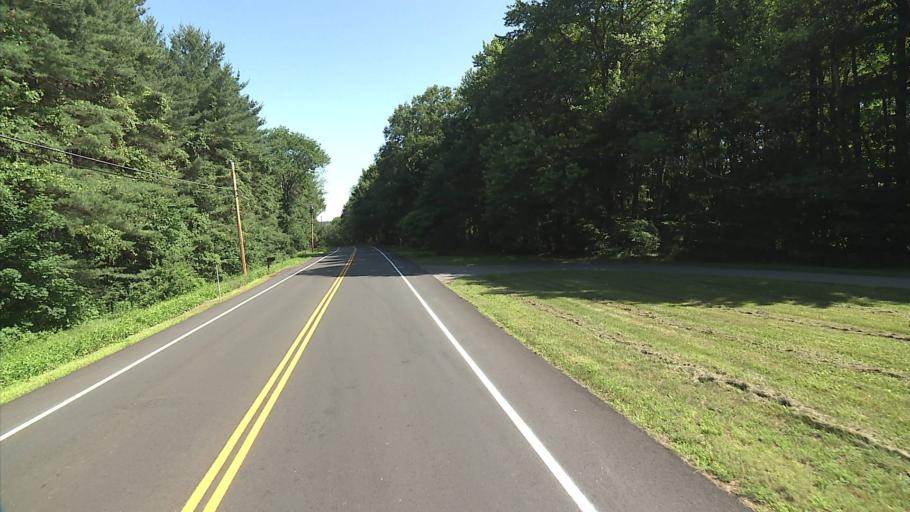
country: US
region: Connecticut
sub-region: Litchfield County
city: Northwest Harwinton
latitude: 41.7681
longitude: -73.0256
